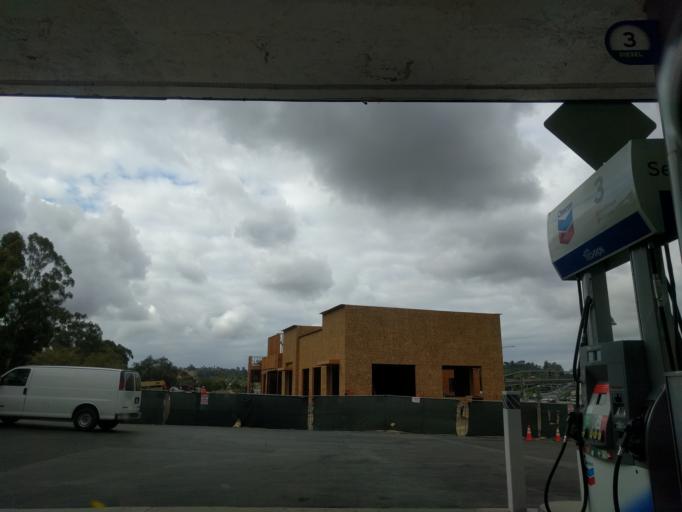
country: US
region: California
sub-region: Orange County
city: Ladera Ranch
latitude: 33.5598
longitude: -117.6709
